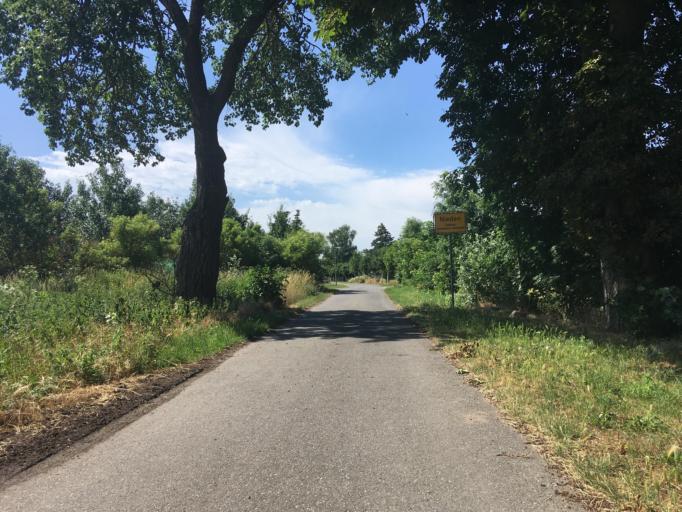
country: DE
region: Brandenburg
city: Goritz
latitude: 53.4432
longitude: 13.9221
